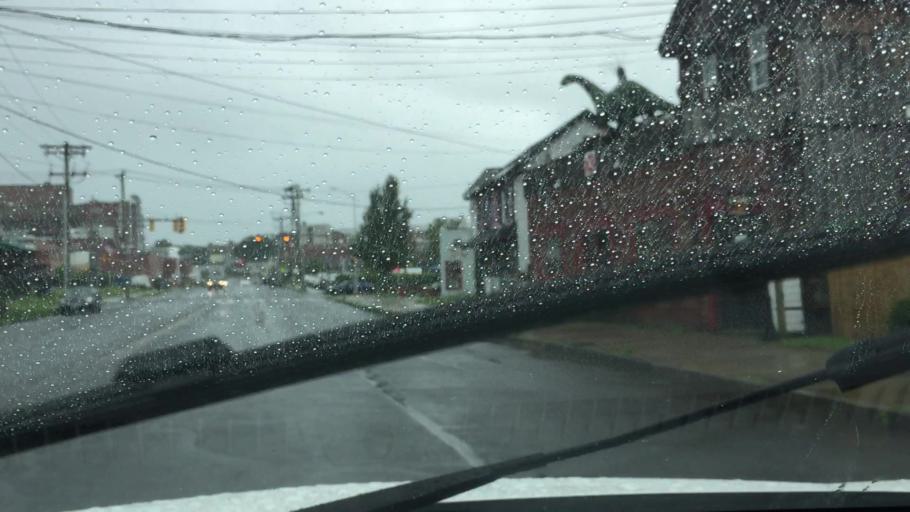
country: US
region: Massachusetts
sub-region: Berkshire County
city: Pittsfield
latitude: 42.4615
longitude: -73.2510
